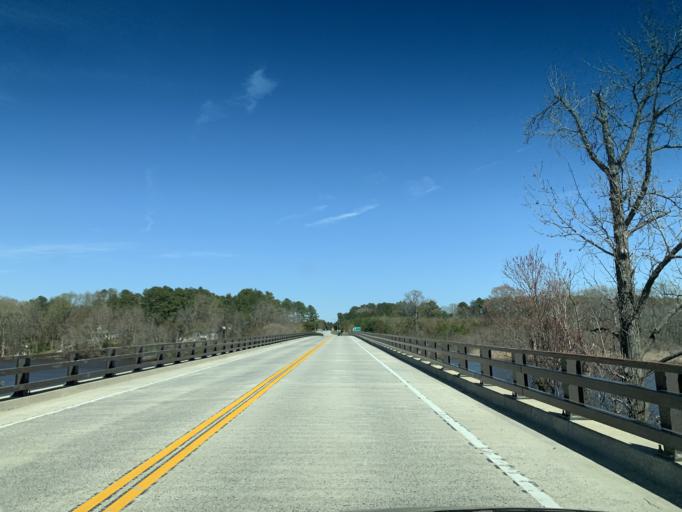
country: US
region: Maryland
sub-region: Caroline County
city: Denton
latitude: 38.8304
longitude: -75.9149
